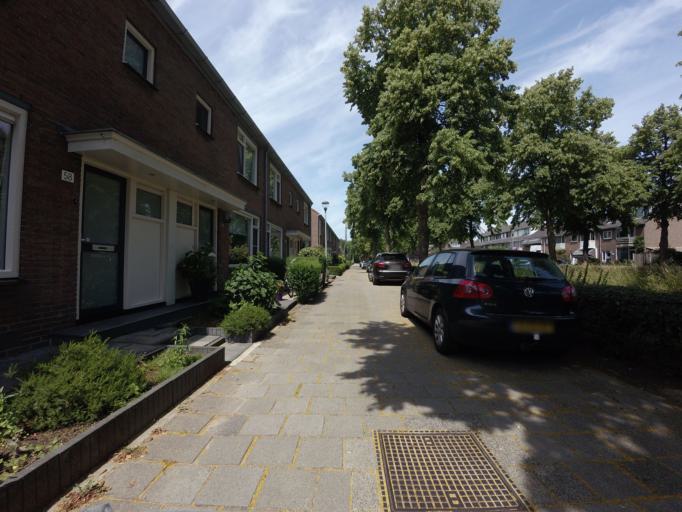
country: NL
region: Utrecht
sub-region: Gemeente Woerden
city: Woerden
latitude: 52.0818
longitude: 4.8724
